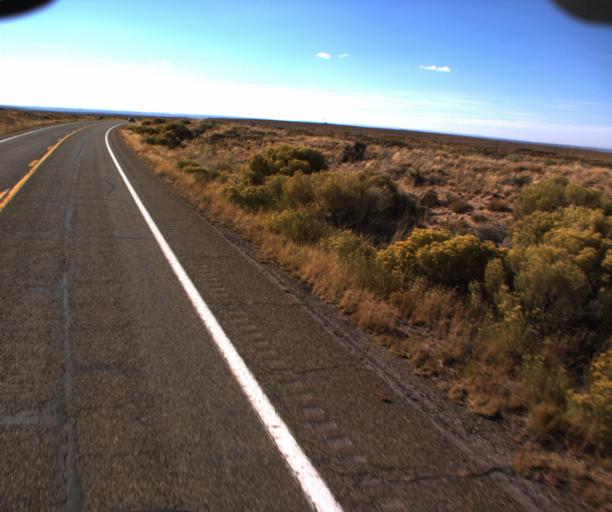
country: US
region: Arizona
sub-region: Coconino County
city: Kaibito
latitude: 36.6122
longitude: -111.0140
